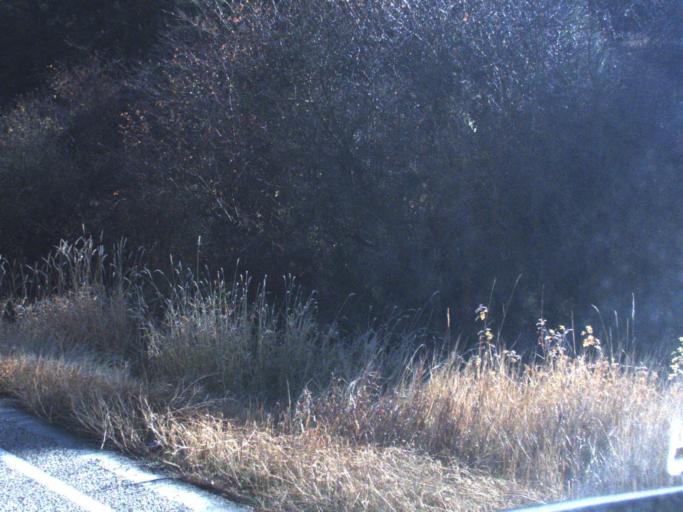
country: US
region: Washington
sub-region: Ferry County
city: Republic
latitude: 48.7782
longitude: -118.6352
